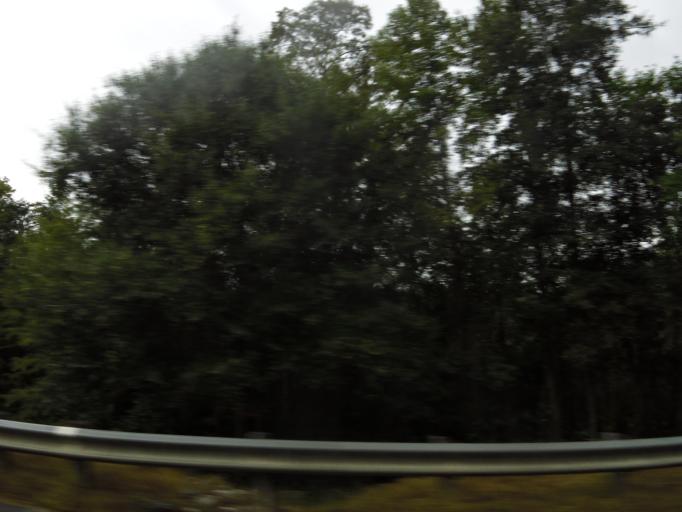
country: US
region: Florida
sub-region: Nassau County
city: Callahan
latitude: 30.5069
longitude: -82.0358
